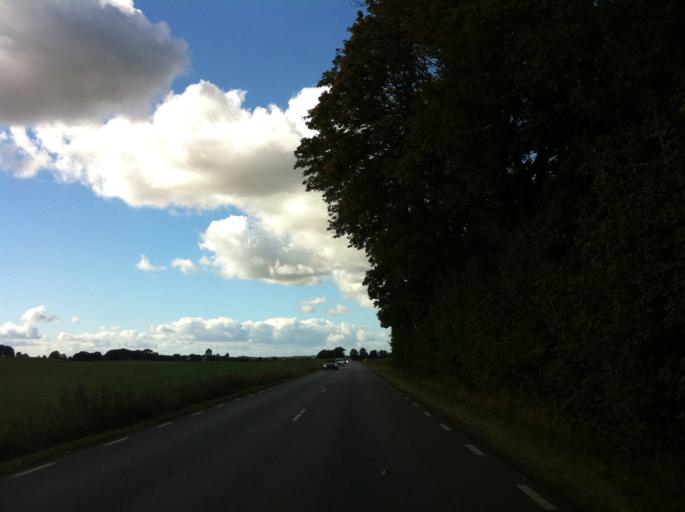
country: SE
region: Skane
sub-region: Tomelilla Kommun
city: Tomelilla
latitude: 55.6423
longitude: 13.9995
